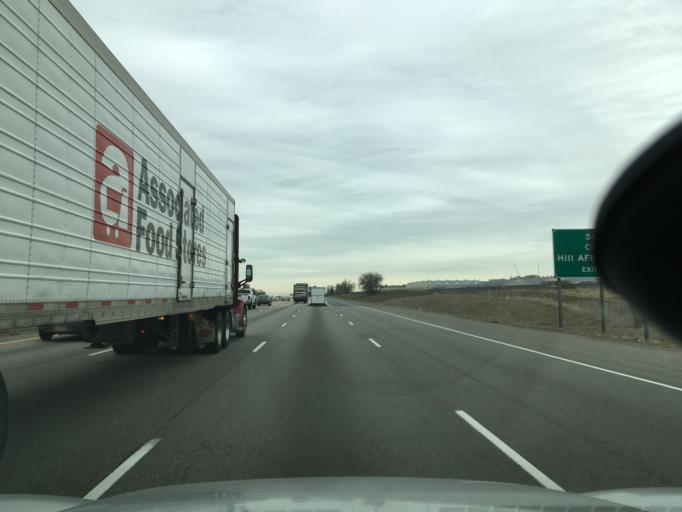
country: US
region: Utah
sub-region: Davis County
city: Clearfield
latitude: 41.1112
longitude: -112.0107
